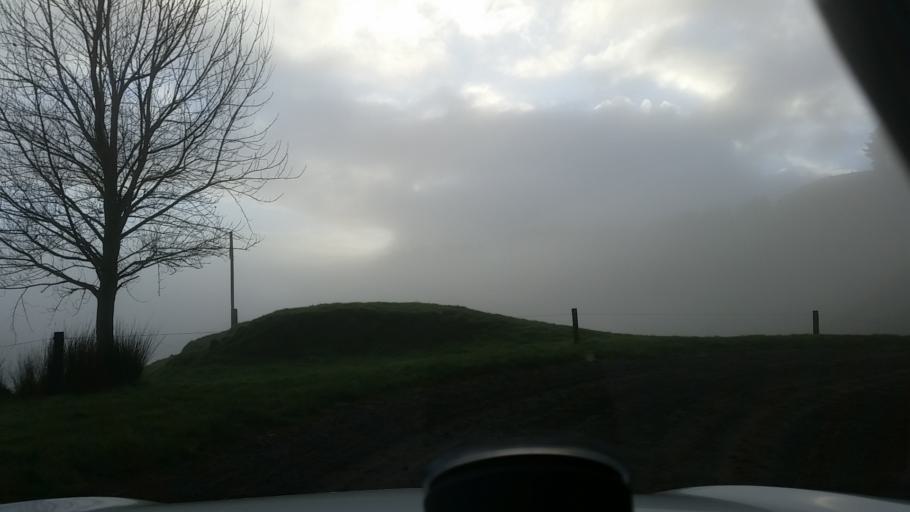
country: NZ
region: Taranaki
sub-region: South Taranaki District
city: Eltham
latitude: -39.4356
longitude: 174.4512
